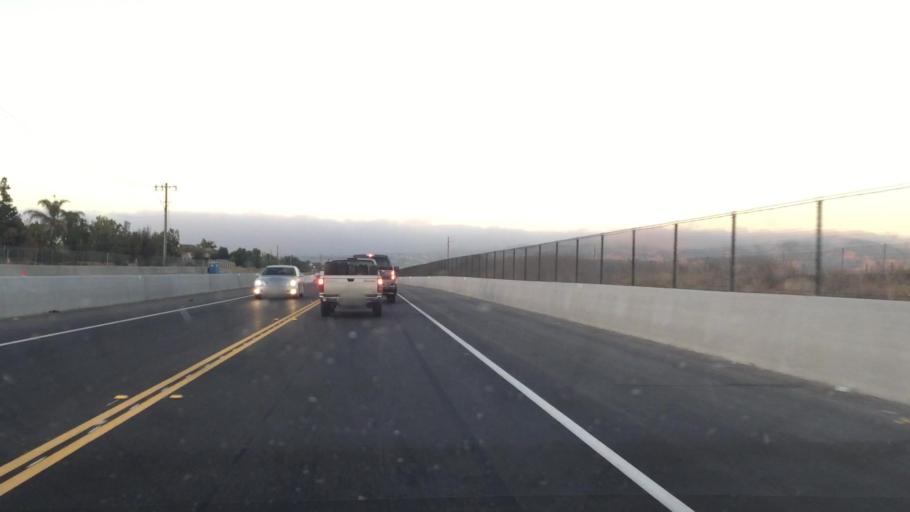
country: US
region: California
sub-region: Alameda County
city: Livermore
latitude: 37.6650
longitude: -121.8056
